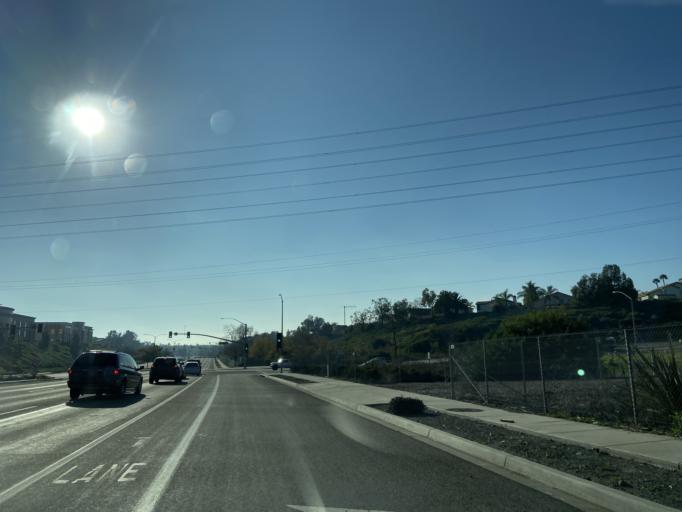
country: US
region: California
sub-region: San Diego County
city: Bonita
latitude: 32.6460
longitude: -116.9713
